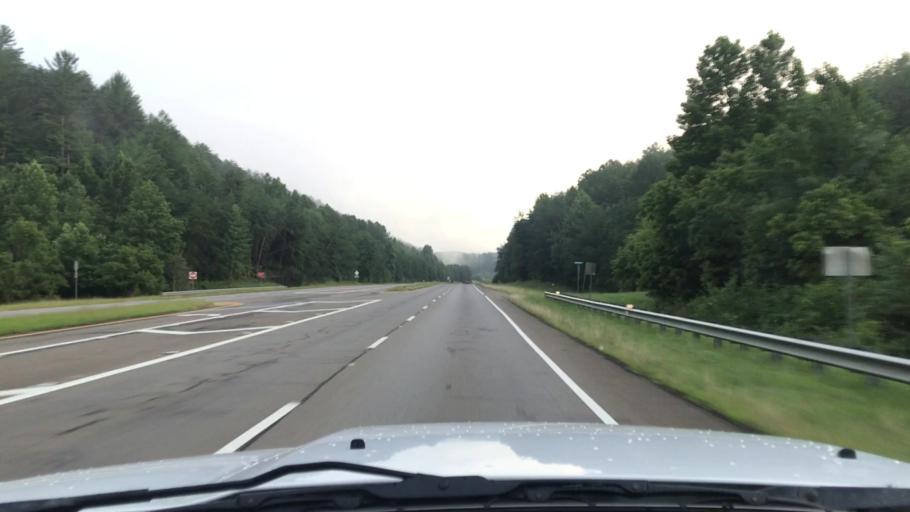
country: US
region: Georgia
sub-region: Gilmer County
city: Ellijay
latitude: 34.6984
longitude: -84.4631
